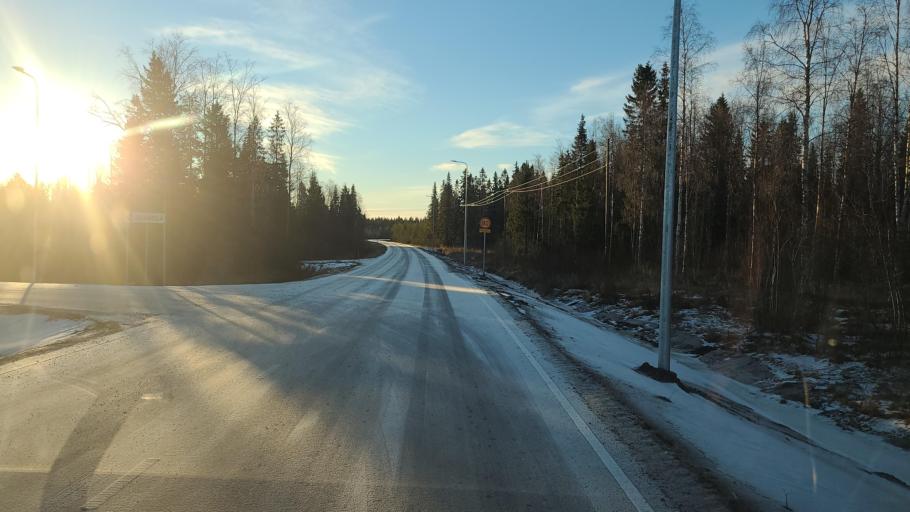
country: FI
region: Lapland
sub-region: Kemi-Tornio
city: Kemi
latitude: 65.6762
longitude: 24.7435
